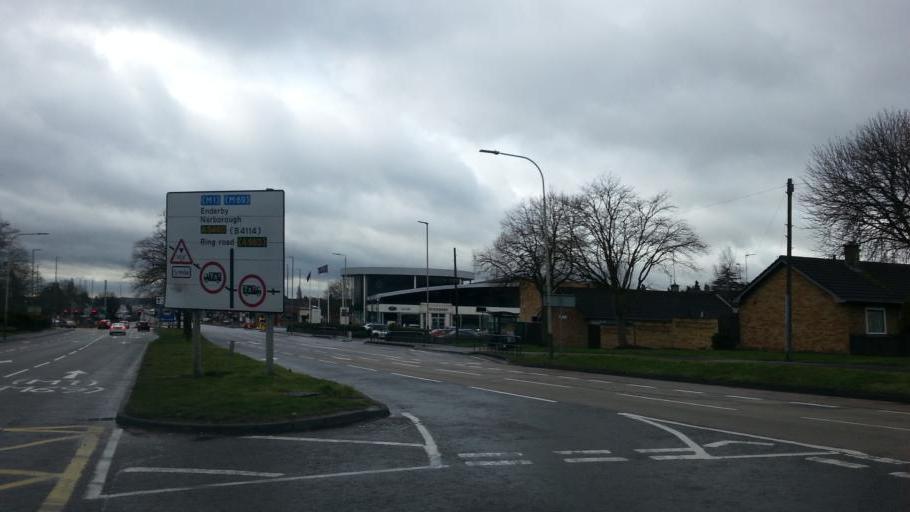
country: GB
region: England
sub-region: Leicestershire
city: Blaby
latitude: 52.6142
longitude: -1.1645
